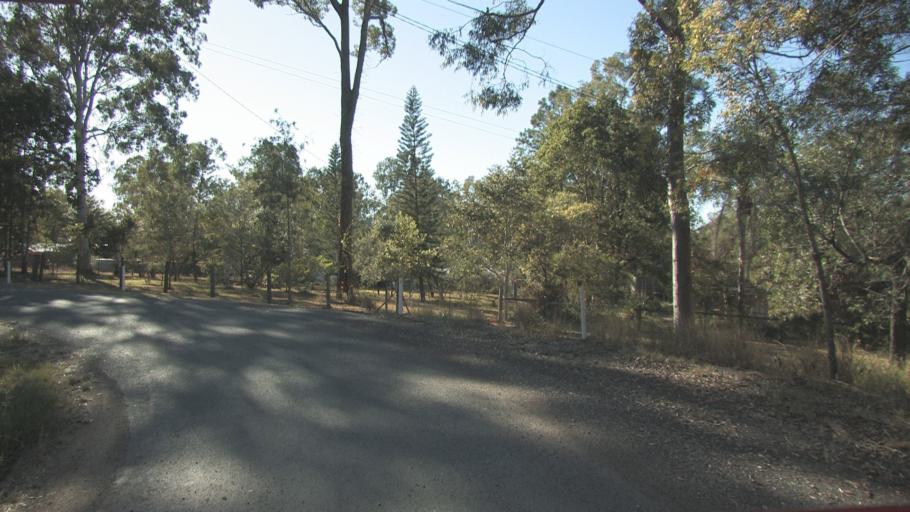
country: AU
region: Queensland
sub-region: Logan
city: North Maclean
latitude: -27.7851
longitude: 152.9851
